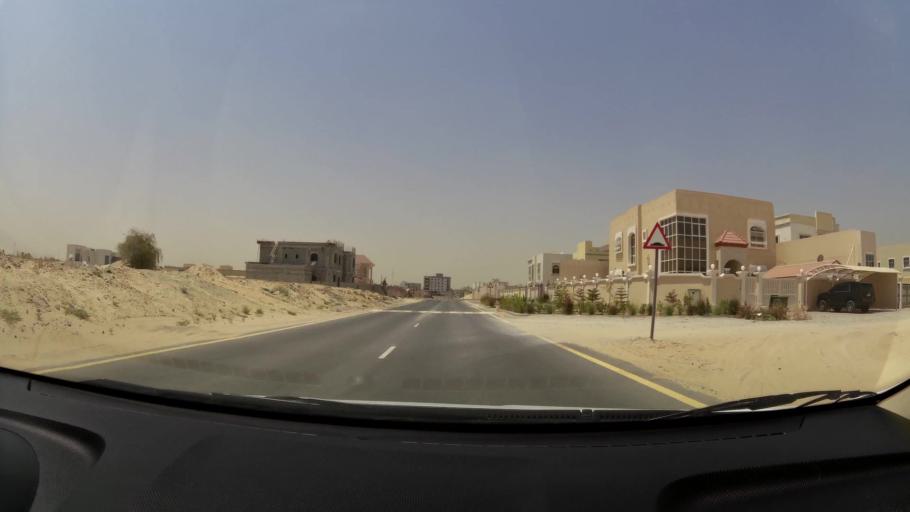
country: AE
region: Ajman
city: Ajman
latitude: 25.4020
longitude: 55.5223
